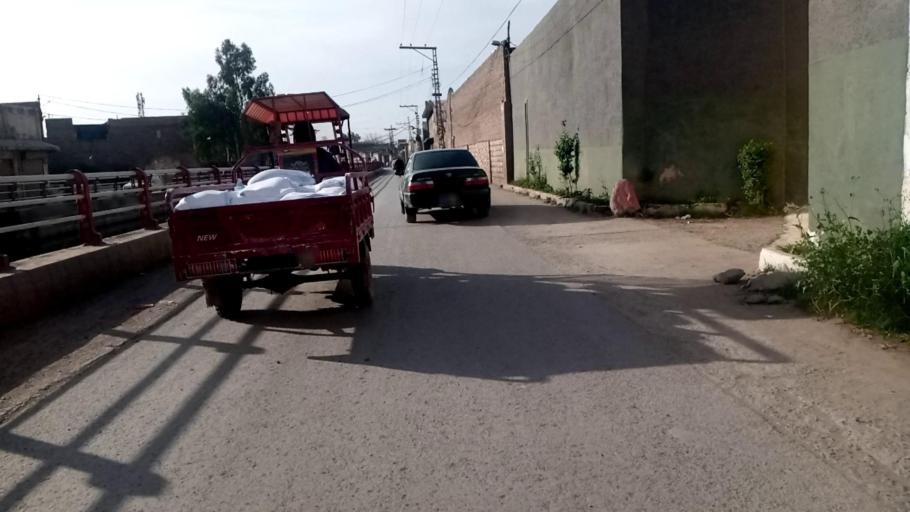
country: PK
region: Khyber Pakhtunkhwa
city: Peshawar
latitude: 34.0147
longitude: 71.6080
